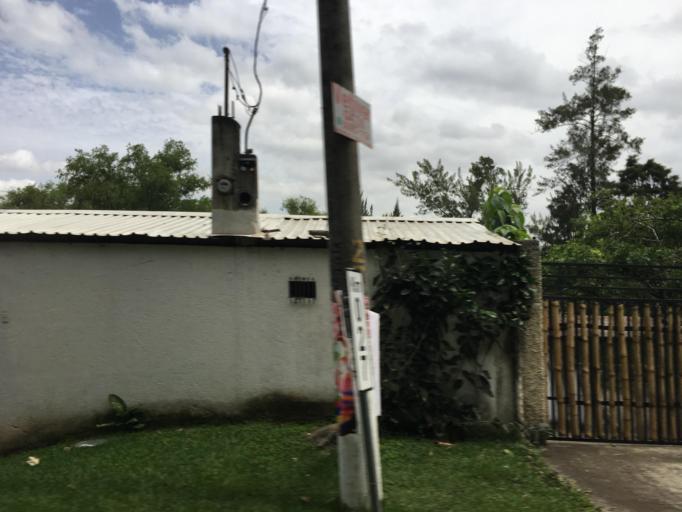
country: GT
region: Guatemala
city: Villa Canales
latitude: 14.4442
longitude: -90.5289
